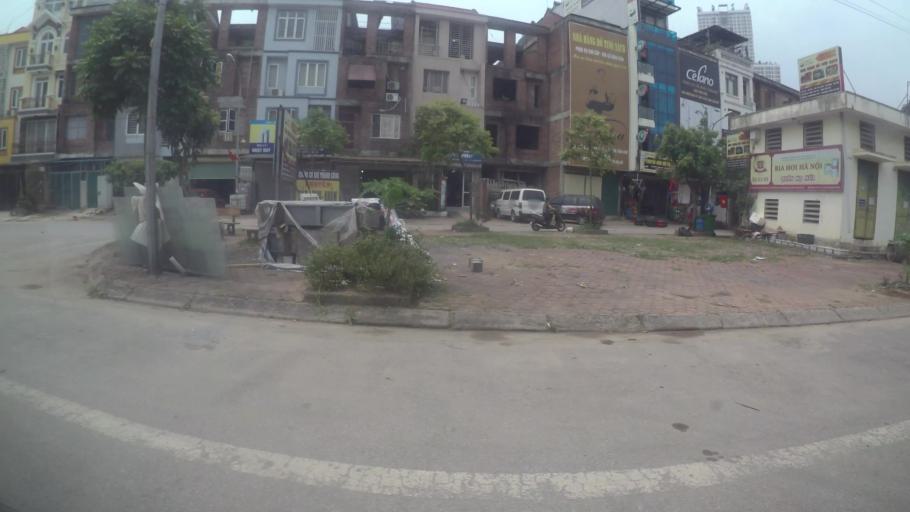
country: VN
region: Ha Noi
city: Ha Dong
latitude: 20.9758
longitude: 105.7662
